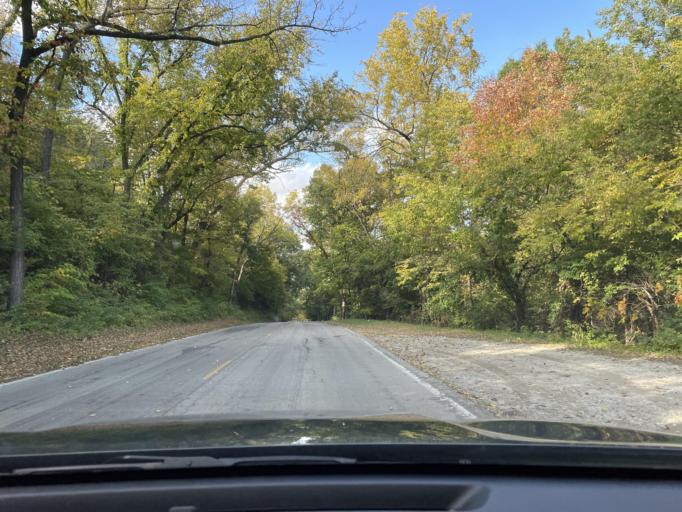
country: US
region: Missouri
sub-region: Buchanan County
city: Saint Joseph
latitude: 39.7301
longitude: -94.8384
